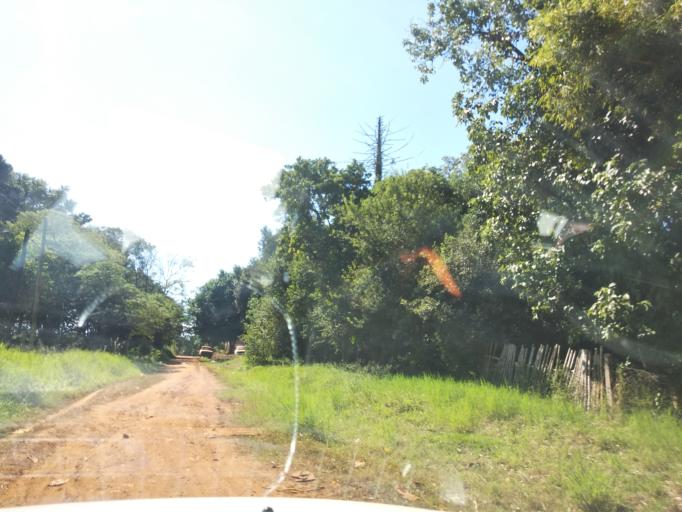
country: AR
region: Misiones
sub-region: Departamento de Capital
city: Posadas
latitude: -27.4305
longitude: -55.8847
